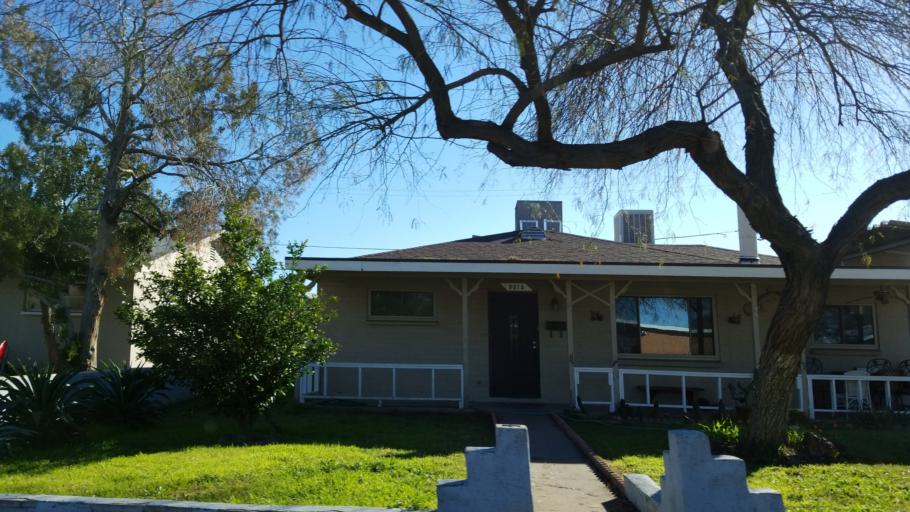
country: US
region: Arizona
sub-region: Maricopa County
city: Glendale
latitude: 33.5663
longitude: -112.1255
